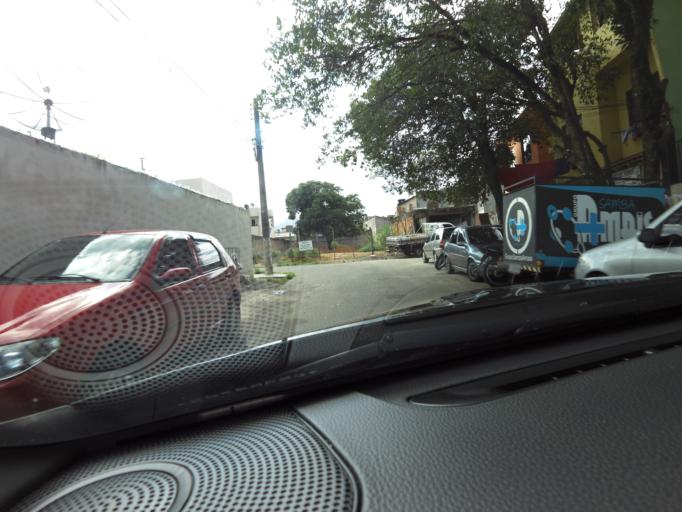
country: BR
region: Espirito Santo
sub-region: Guarapari
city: Guarapari
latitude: -20.6644
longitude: -40.5021
